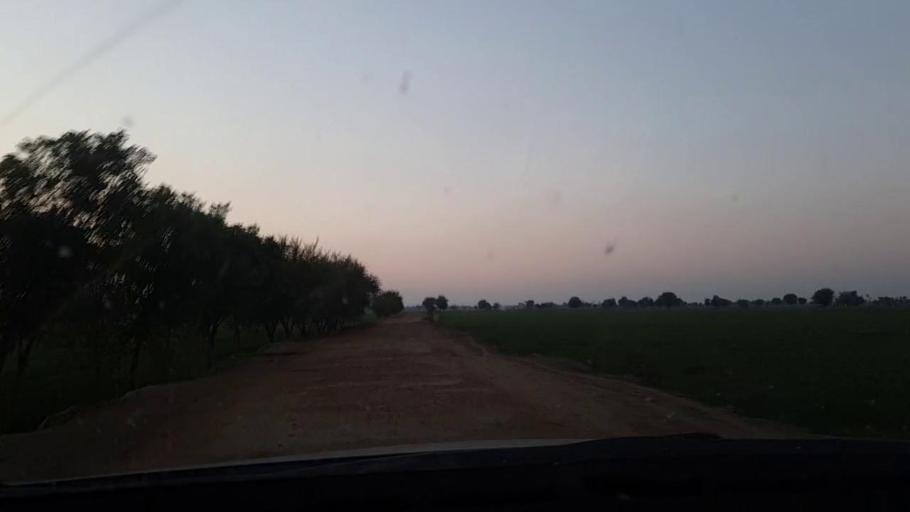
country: PK
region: Sindh
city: Tando Mittha Khan
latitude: 25.9305
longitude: 69.3272
